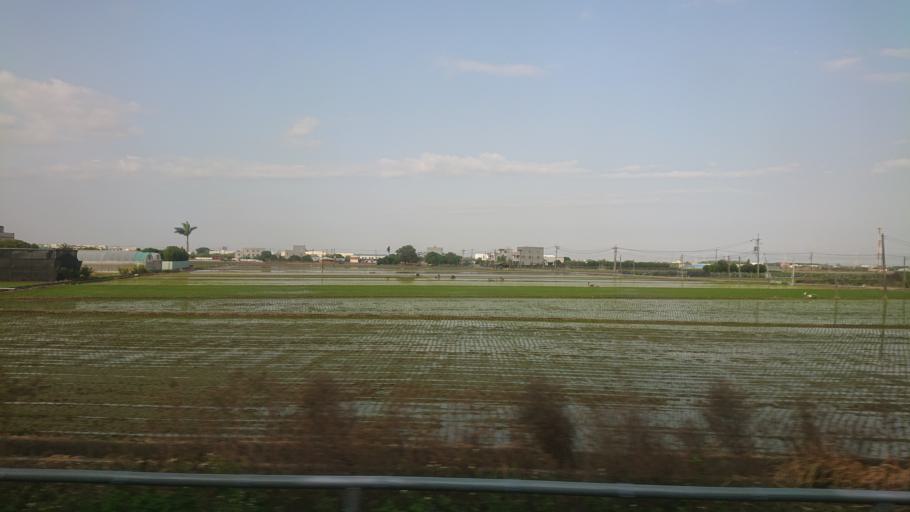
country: TW
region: Taiwan
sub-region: Chiayi
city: Jiayi Shi
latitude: 23.5729
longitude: 120.4365
